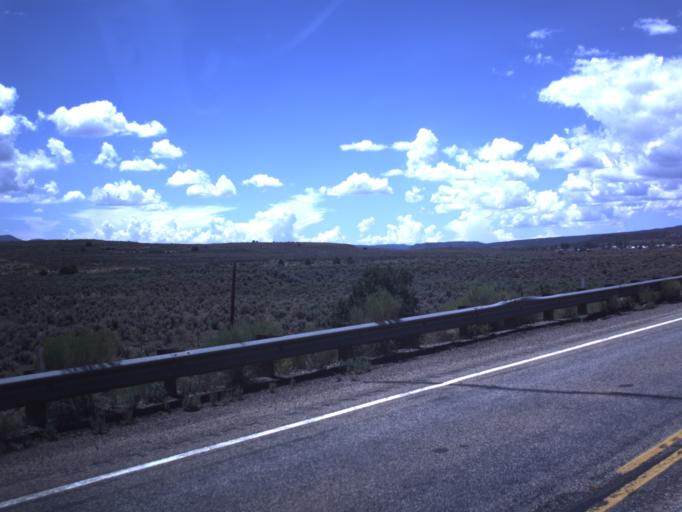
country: US
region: Utah
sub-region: Garfield County
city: Panguitch
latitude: 37.6704
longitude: -112.4129
